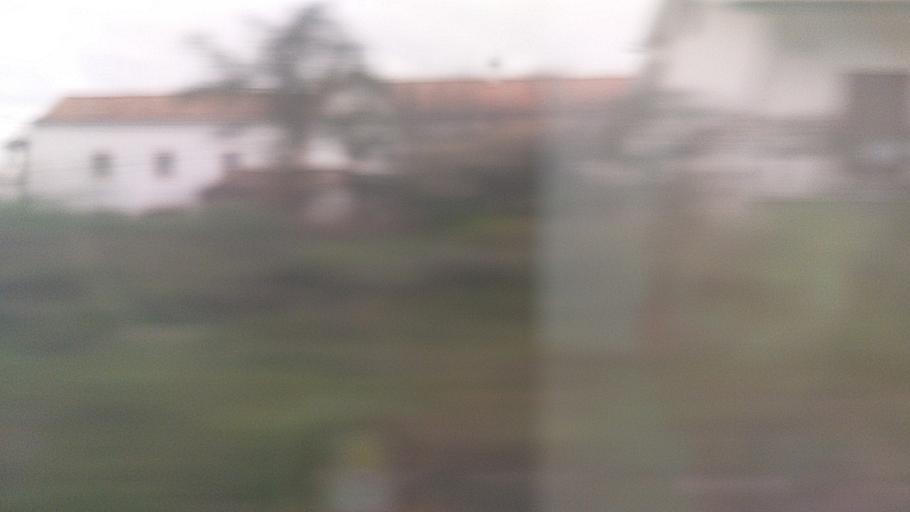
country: PT
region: Coimbra
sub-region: Coimbra
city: Coimbra
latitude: 40.2146
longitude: -8.4573
